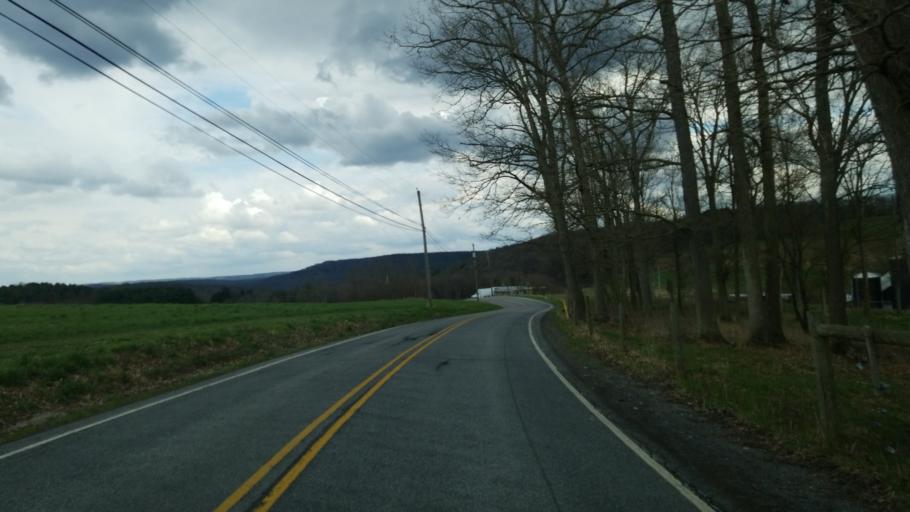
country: US
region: Pennsylvania
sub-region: Clearfield County
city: Curwensville
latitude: 40.8959
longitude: -78.4814
